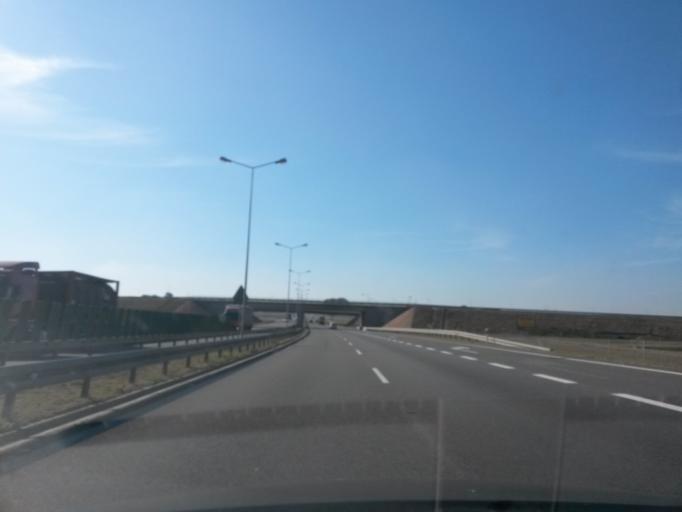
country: PL
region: Opole Voivodeship
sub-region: Powiat strzelecki
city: Strzelce Opolskie
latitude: 50.4592
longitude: 18.2754
